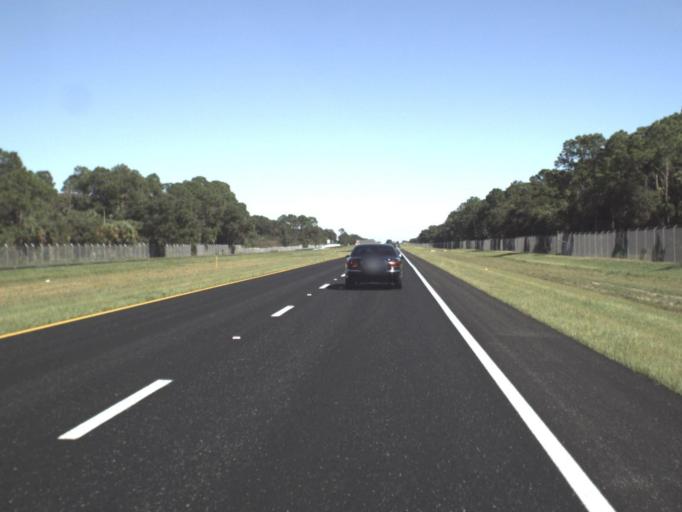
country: US
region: Florida
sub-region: Hendry County
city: Port LaBelle
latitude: 26.7683
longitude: -81.3307
